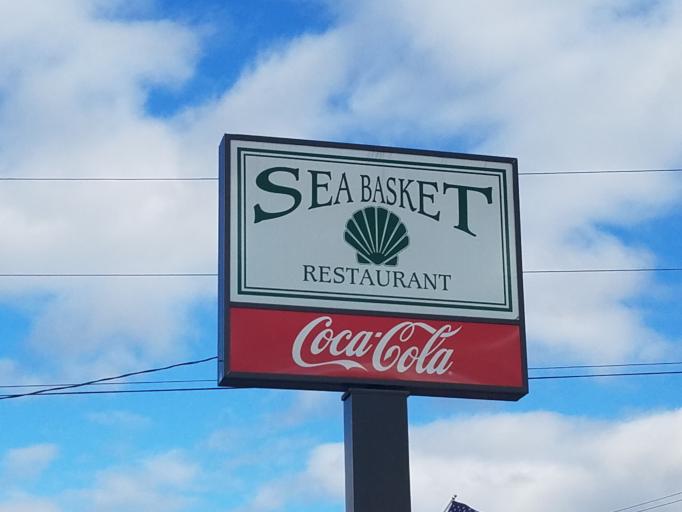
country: US
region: Maine
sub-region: Lincoln County
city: Wiscasset
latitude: 43.9943
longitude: -69.6862
